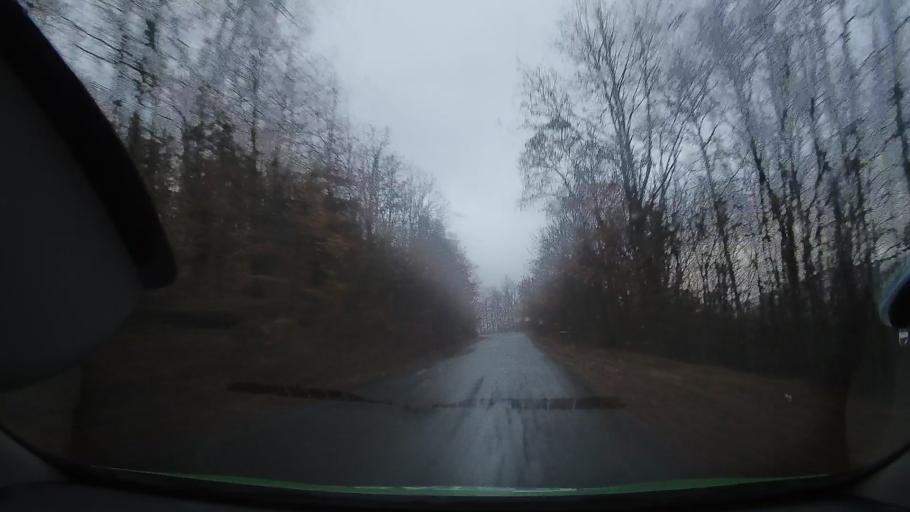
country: RO
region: Hunedoara
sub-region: Comuna Ribita
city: Ribita
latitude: 46.2359
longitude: 22.7483
